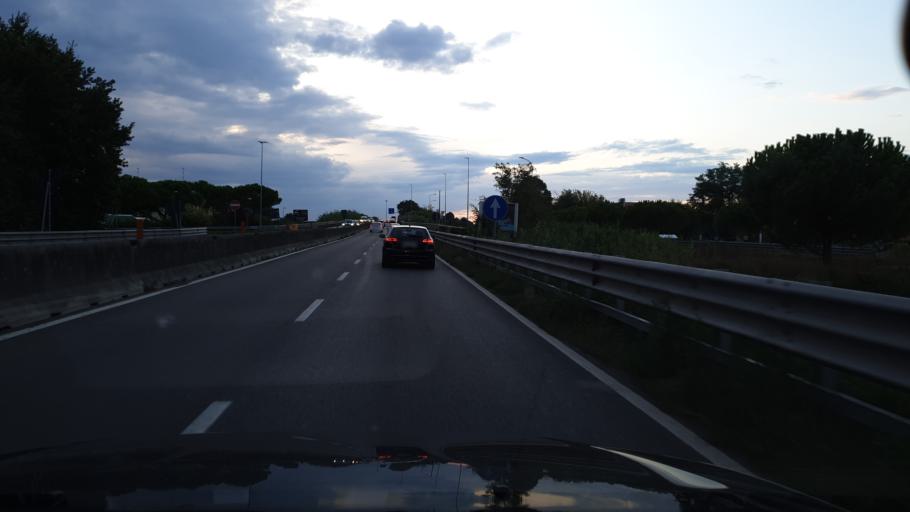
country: IT
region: Emilia-Romagna
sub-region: Provincia di Ravenna
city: Madonna Dell'Albero
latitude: 44.3822
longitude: 12.2010
